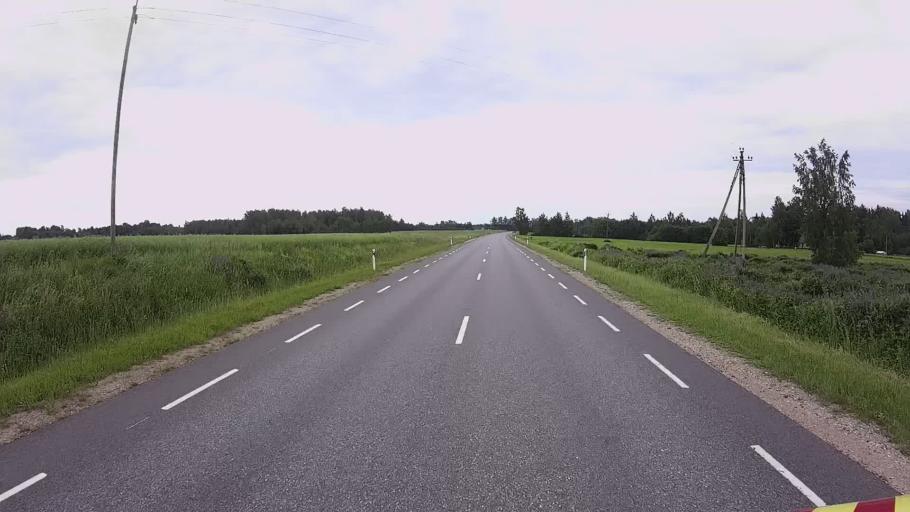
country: EE
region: Viljandimaa
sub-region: Karksi vald
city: Karksi-Nuia
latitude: 58.1665
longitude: 25.5822
